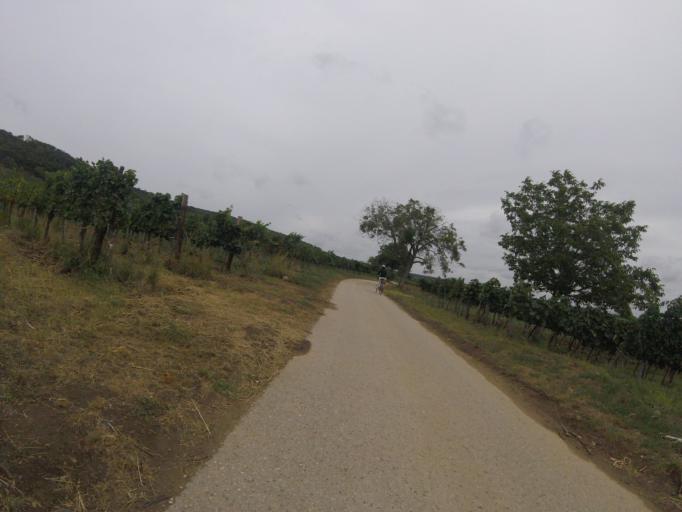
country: AT
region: Burgenland
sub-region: Politischer Bezirk Neusiedl am See
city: Jois
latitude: 47.9712
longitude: 16.7718
